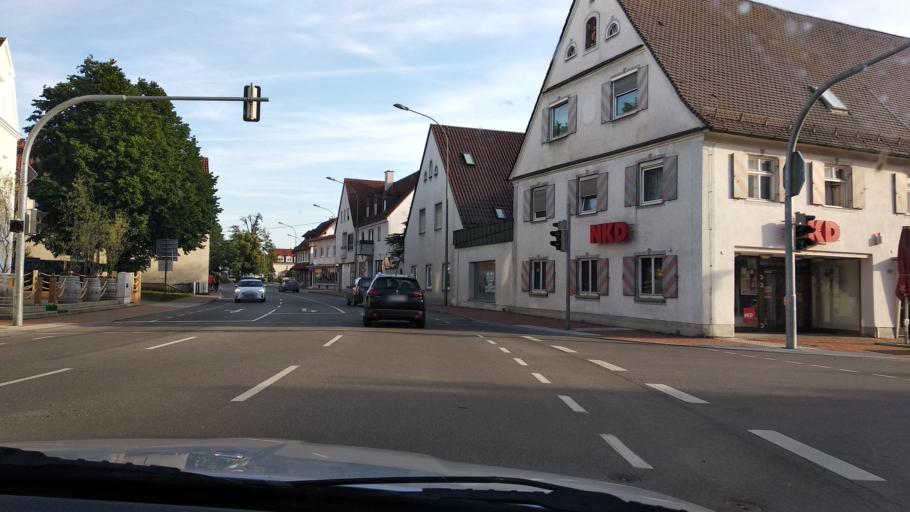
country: DE
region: Bavaria
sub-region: Swabia
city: Illertissen
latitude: 48.2228
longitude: 10.1029
